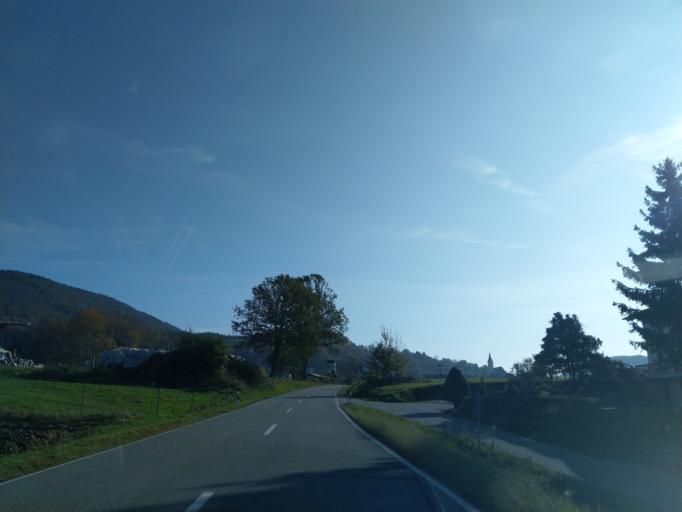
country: DE
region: Bavaria
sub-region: Lower Bavaria
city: Grattersdorf
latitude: 48.8075
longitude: 13.1447
